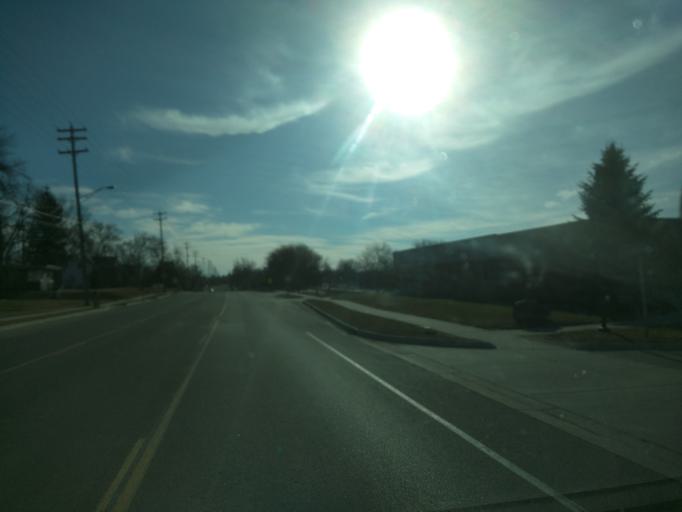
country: US
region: Michigan
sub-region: Ingham County
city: Edgemont Park
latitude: 42.7338
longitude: -84.5937
